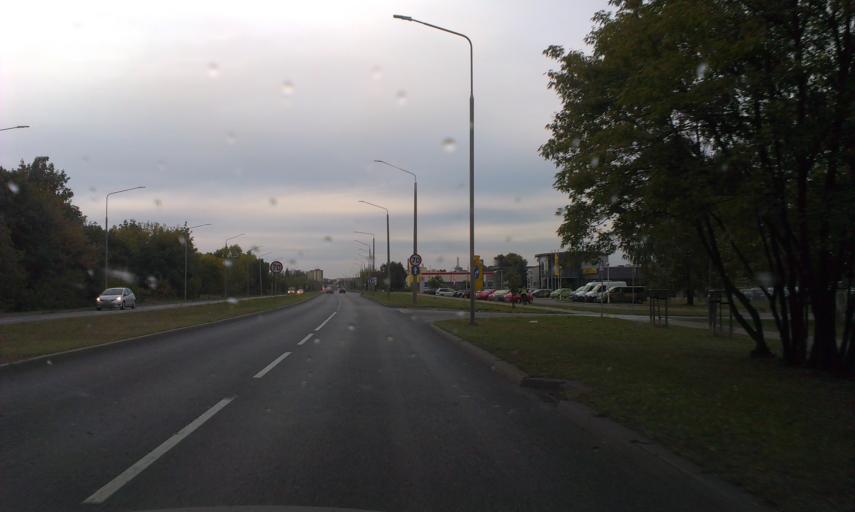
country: PL
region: Masovian Voivodeship
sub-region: Radom
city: Radom
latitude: 51.4191
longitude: 21.1392
